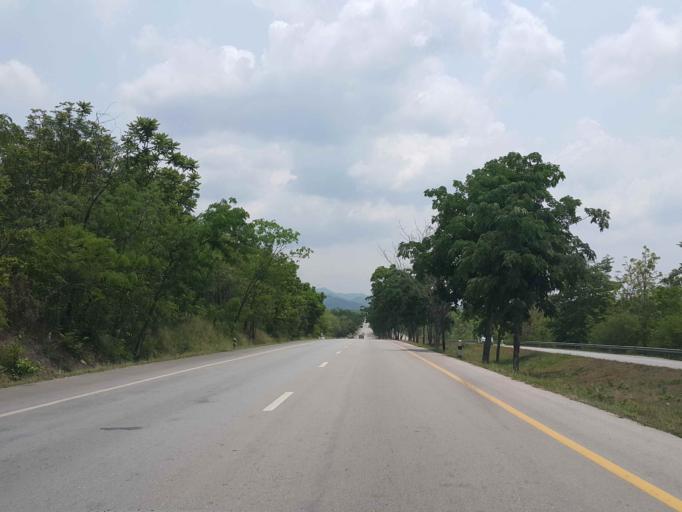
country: TH
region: Lampang
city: Ko Kha
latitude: 18.1276
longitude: 99.3915
